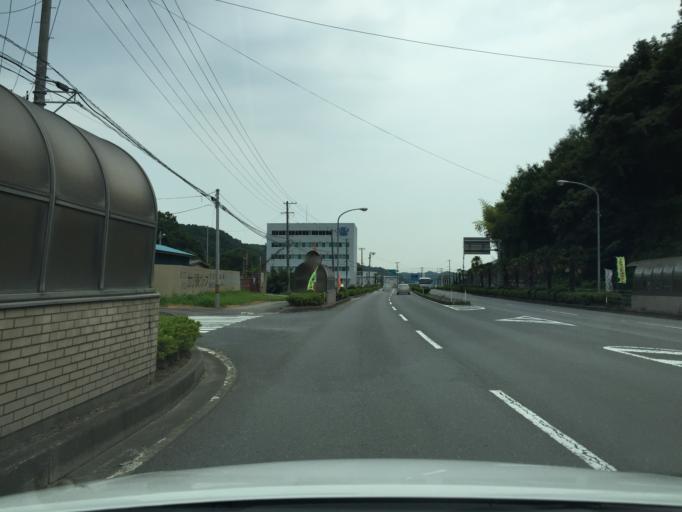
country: JP
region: Fukushima
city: Iwaki
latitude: 36.9995
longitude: 140.8216
